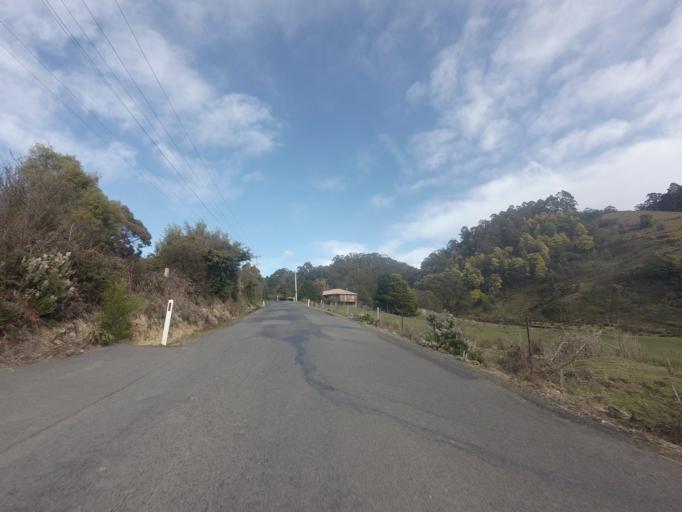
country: AU
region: Tasmania
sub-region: Kingborough
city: Margate
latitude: -42.9950
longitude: 147.1822
